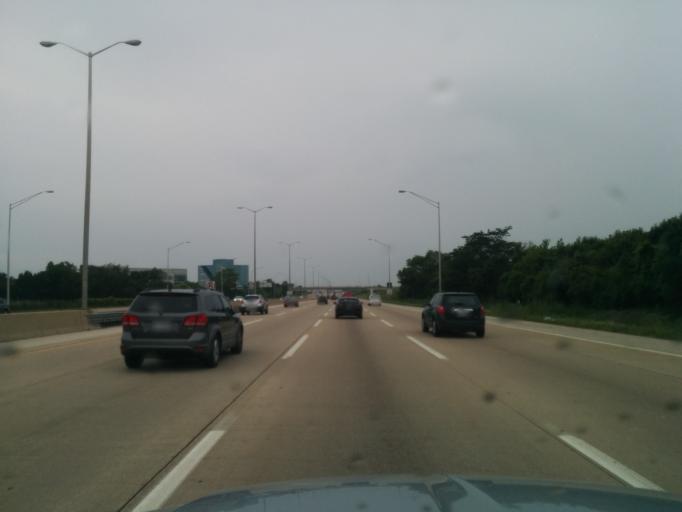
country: US
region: Illinois
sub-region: DuPage County
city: Naperville
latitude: 41.8064
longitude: -88.1351
